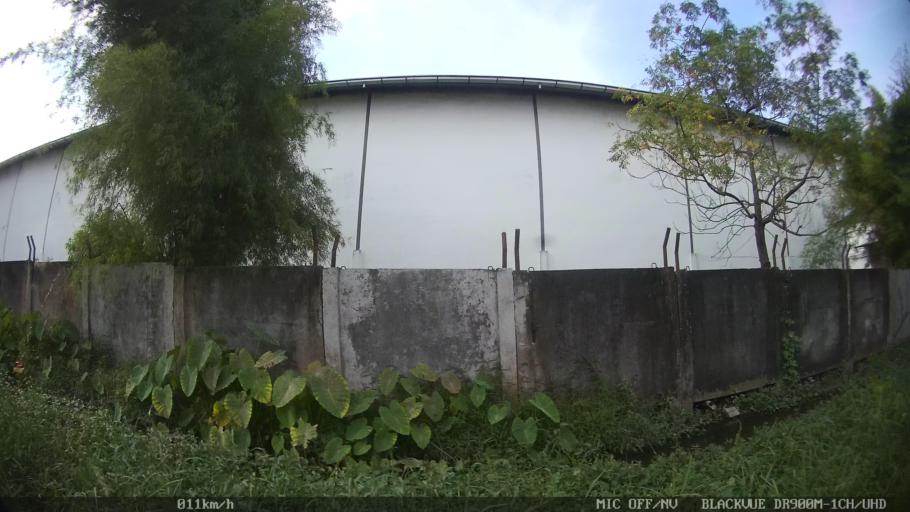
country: ID
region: North Sumatra
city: Medan
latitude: 3.6055
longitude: 98.7378
